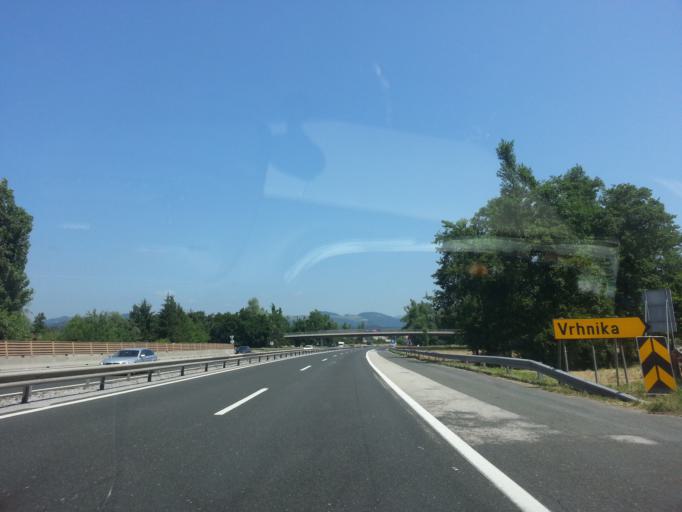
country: SI
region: Vrhnika
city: Verd
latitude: 45.9662
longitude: 14.3048
